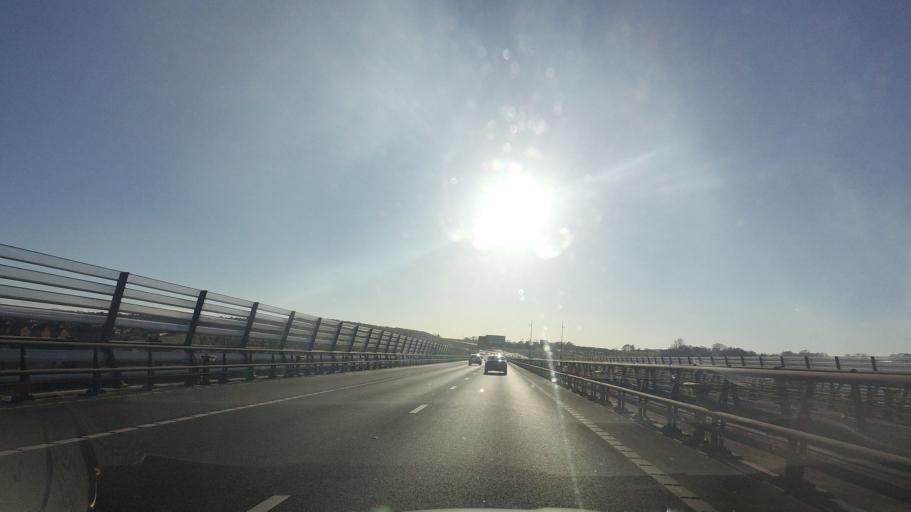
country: GB
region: Scotland
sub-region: Edinburgh
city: Queensferry
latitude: 55.9937
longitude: -3.4191
